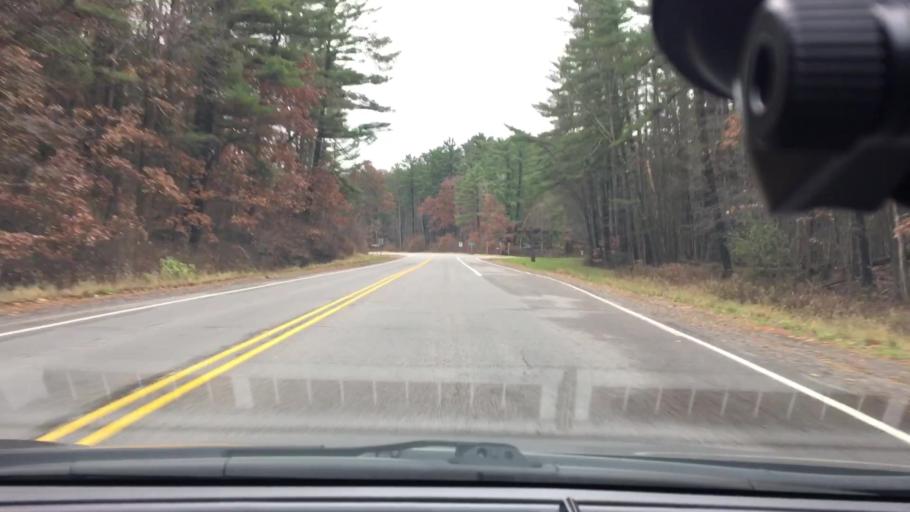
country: US
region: Wisconsin
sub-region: Columbia County
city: Wisconsin Dells
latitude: 43.6421
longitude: -89.8029
